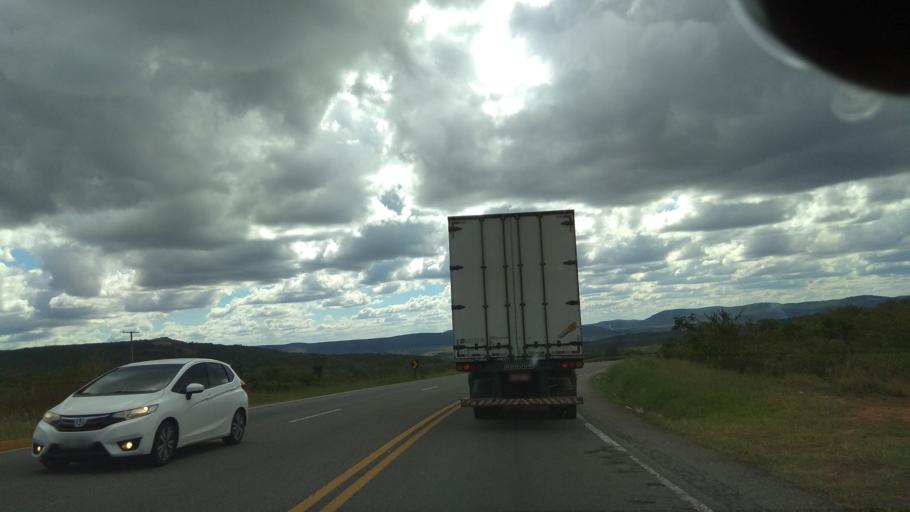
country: BR
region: Bahia
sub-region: Santa Ines
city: Santa Ines
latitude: -13.0429
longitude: -39.9670
